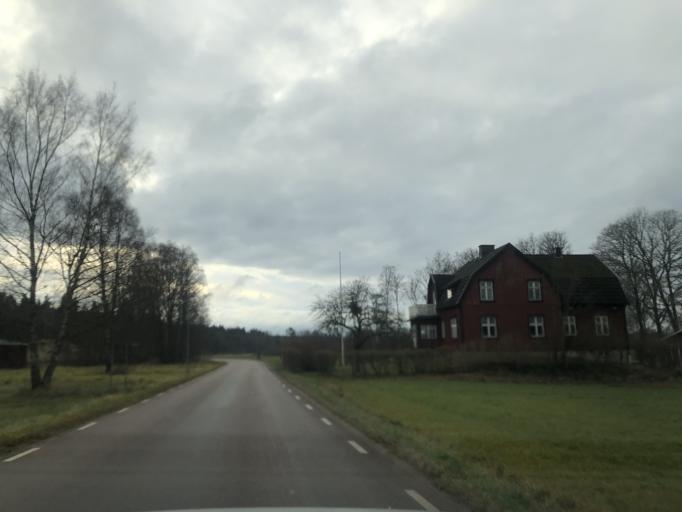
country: SE
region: Vaestra Goetaland
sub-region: Boras Kommun
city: Dalsjofors
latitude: 57.8246
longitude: 13.1574
